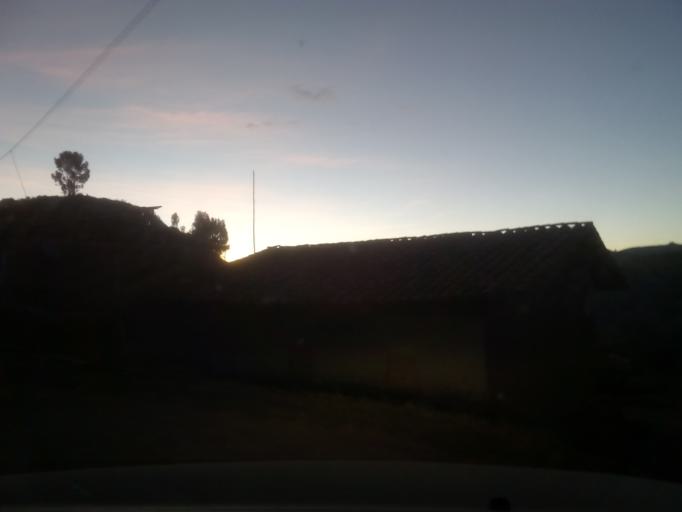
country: PE
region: La Libertad
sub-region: Provincia de Otuzco
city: Mache
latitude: -8.0348
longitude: -78.4588
